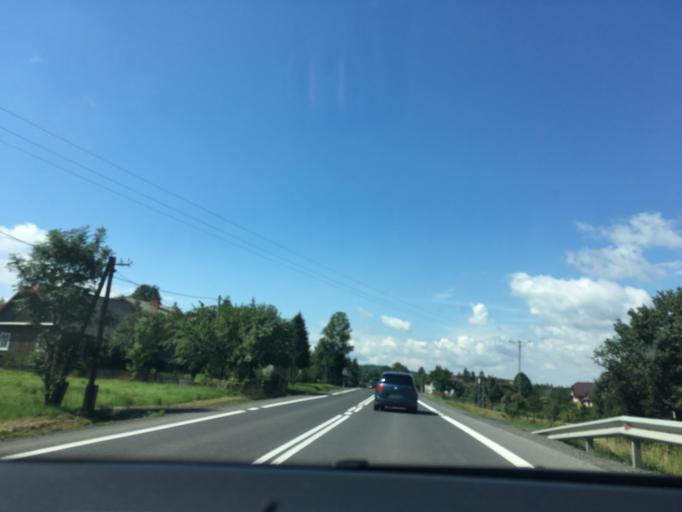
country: PL
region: Subcarpathian Voivodeship
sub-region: Powiat krosnienski
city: Dukla
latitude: 49.5382
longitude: 21.6940
